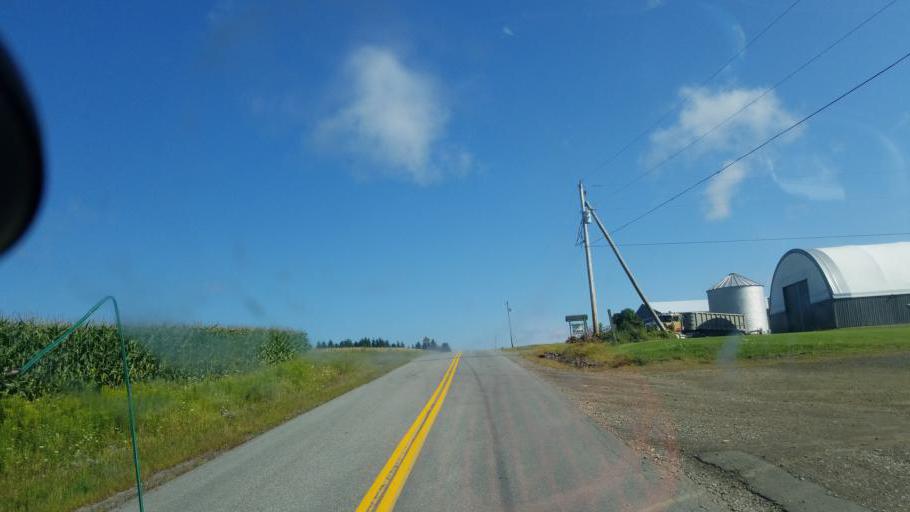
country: US
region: New York
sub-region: Allegany County
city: Andover
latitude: 42.1540
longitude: -77.7136
